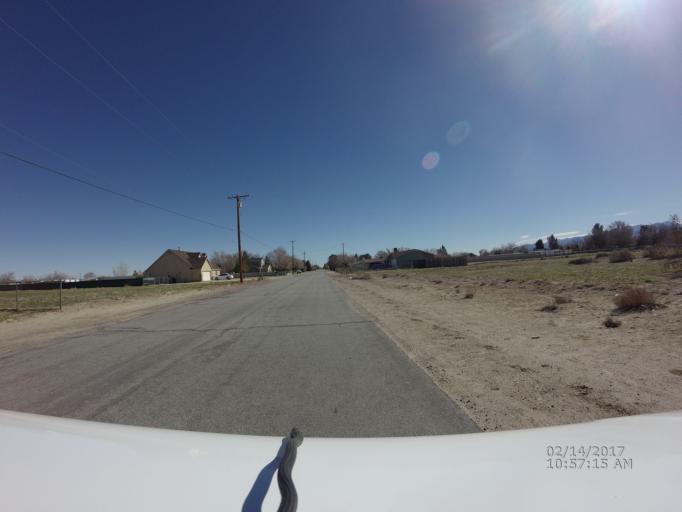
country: US
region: California
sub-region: Los Angeles County
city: Littlerock
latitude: 34.5706
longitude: -117.9459
